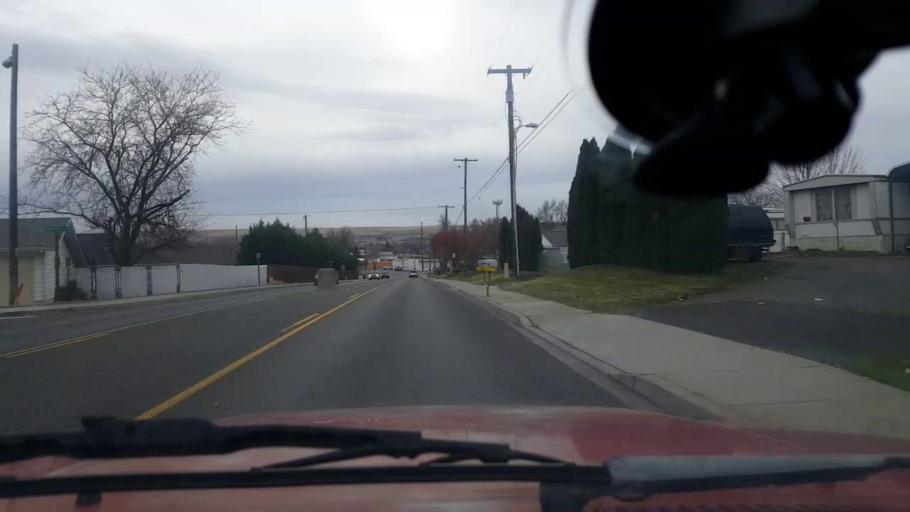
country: US
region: Washington
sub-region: Asotin County
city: Clarkston Heights-Vineland
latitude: 46.3987
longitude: -117.0815
